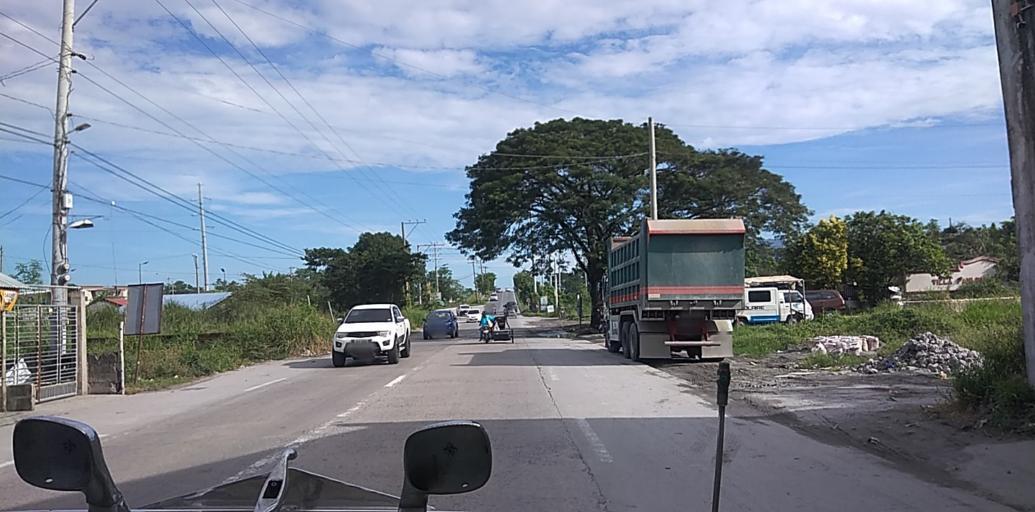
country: PH
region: Central Luzon
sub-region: Province of Pampanga
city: Acli
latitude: 15.1060
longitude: 120.6603
